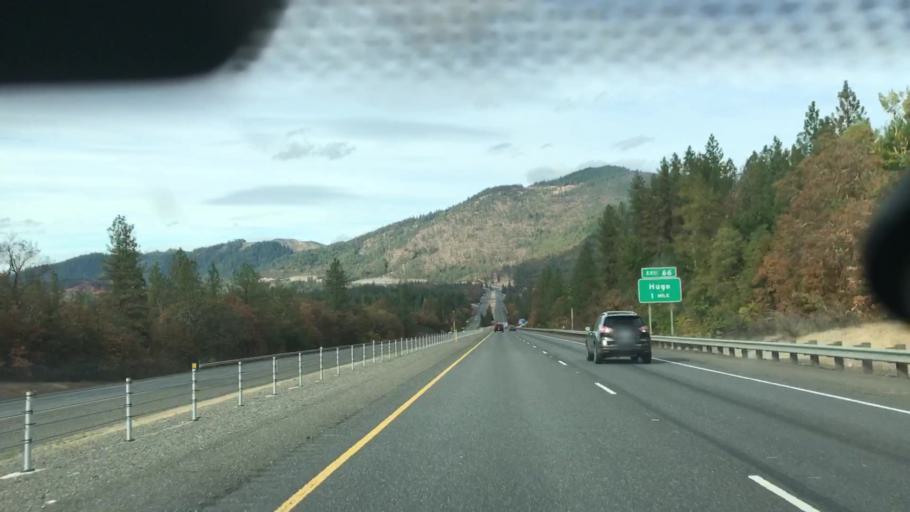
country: US
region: Oregon
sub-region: Josephine County
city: Merlin
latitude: 42.5493
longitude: -123.3707
